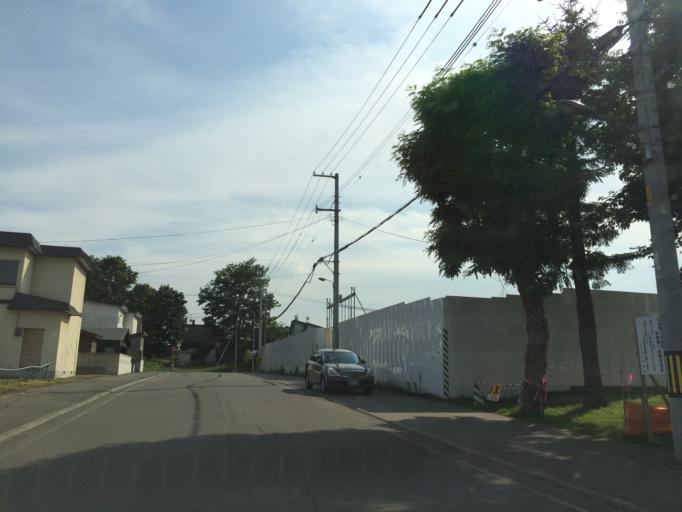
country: JP
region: Hokkaido
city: Ebetsu
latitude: 43.1141
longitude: 141.5500
